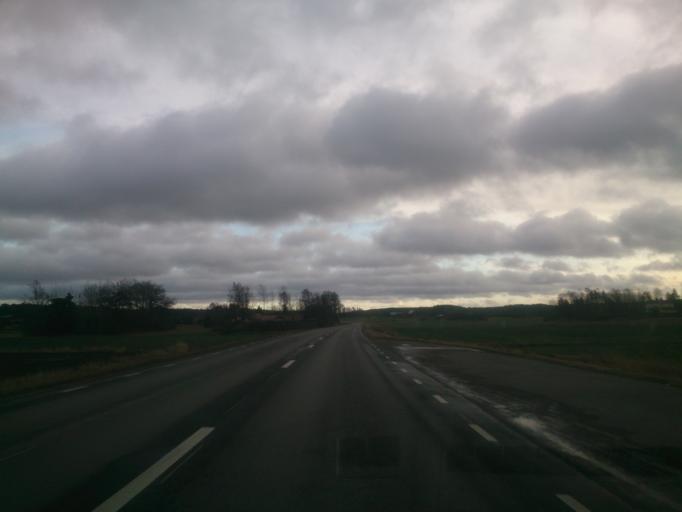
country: SE
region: OEstergoetland
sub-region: Norrkopings Kommun
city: Krokek
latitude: 58.5731
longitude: 16.4146
